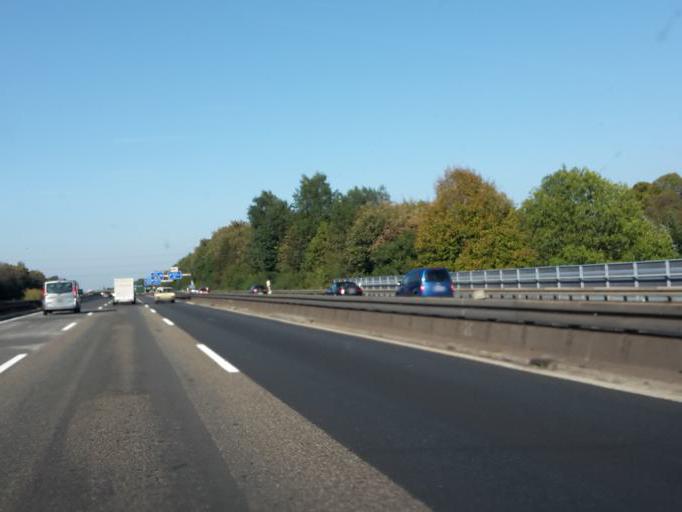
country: DE
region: North Rhine-Westphalia
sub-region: Regierungsbezirk Arnsberg
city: Holzwickede
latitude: 51.5159
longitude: 7.6553
